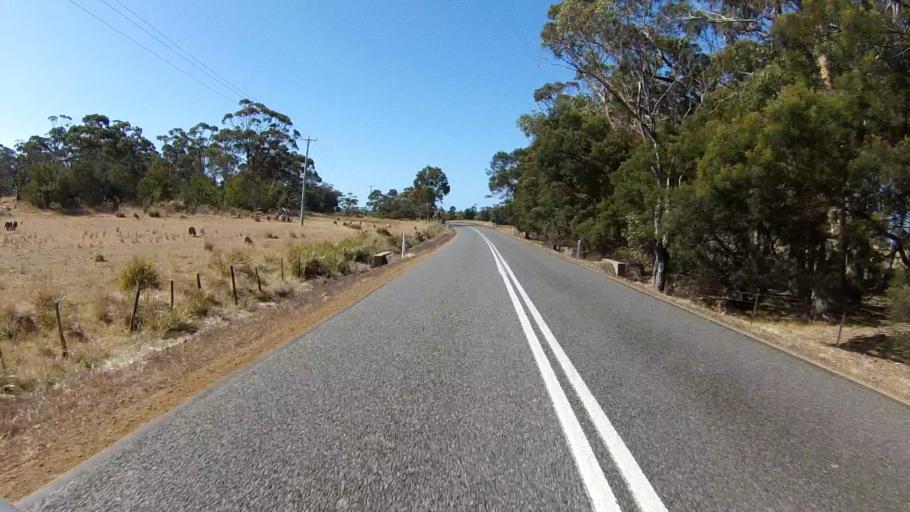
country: AU
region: Tasmania
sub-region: Sorell
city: Sorell
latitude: -42.2892
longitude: 147.9940
